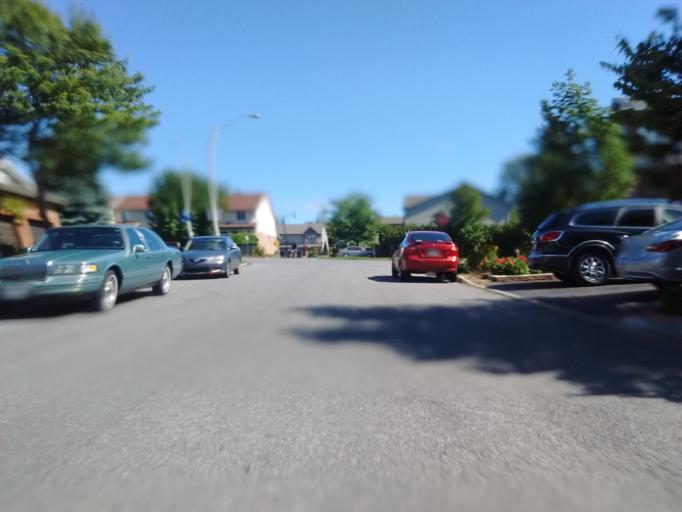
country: CA
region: Ontario
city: Ottawa
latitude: 45.4409
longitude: -75.6342
